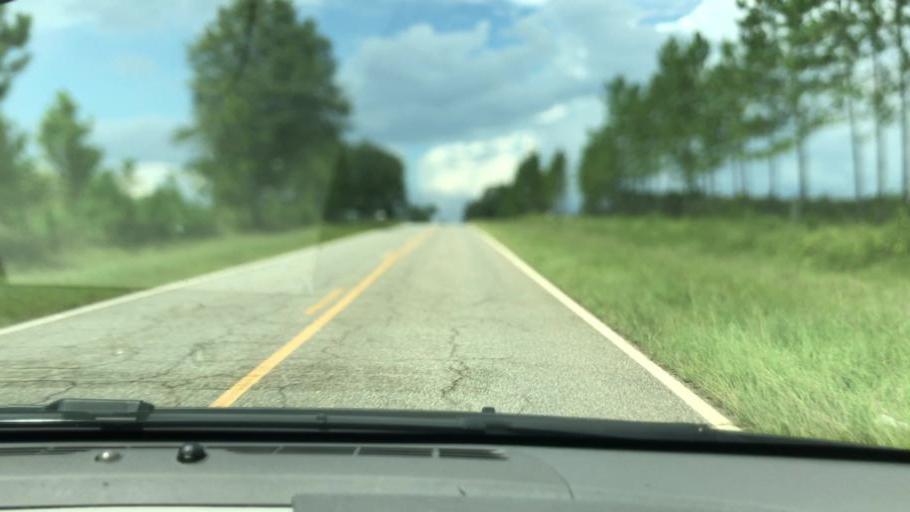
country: US
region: Georgia
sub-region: Early County
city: Blakely
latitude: 31.2708
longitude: -84.9906
